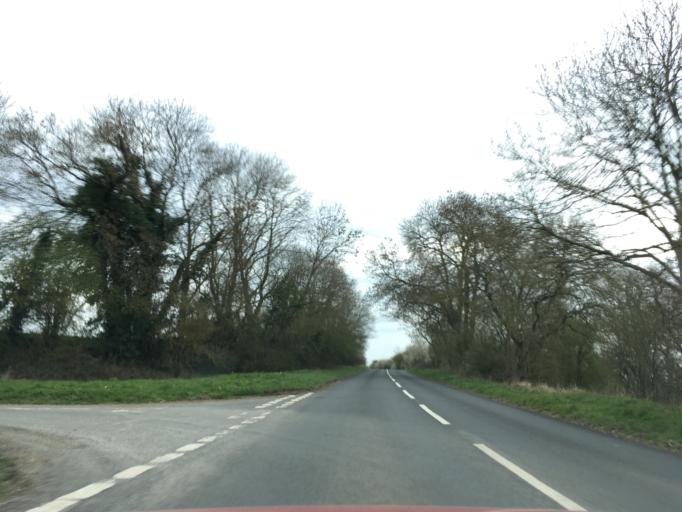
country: GB
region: England
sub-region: Gloucestershire
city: Northleach
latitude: 51.7848
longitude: -1.7798
